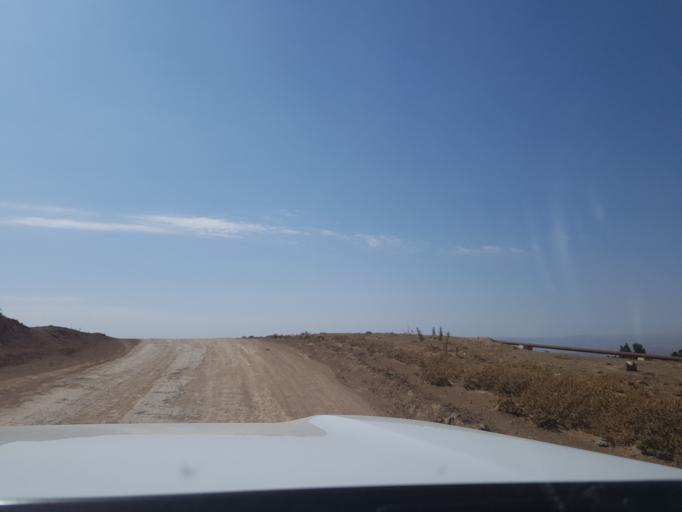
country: TM
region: Ahal
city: Baharly
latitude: 38.3218
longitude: 56.9531
